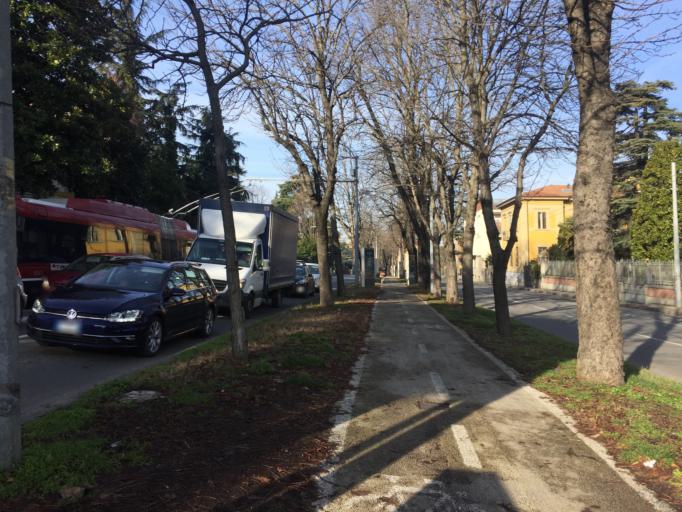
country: IT
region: Emilia-Romagna
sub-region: Provincia di Bologna
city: Bologna
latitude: 44.4888
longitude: 11.3334
